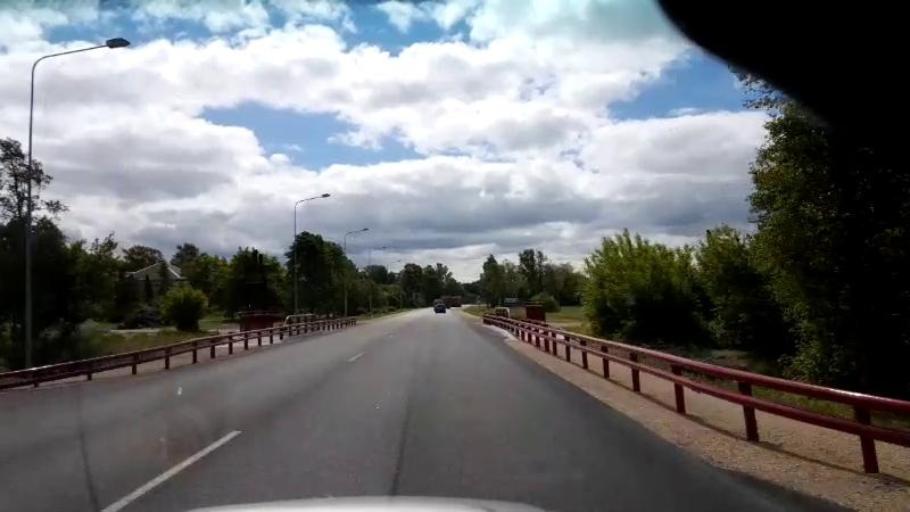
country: LV
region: Salacgrivas
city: Salacgriva
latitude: 57.7871
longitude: 24.3546
